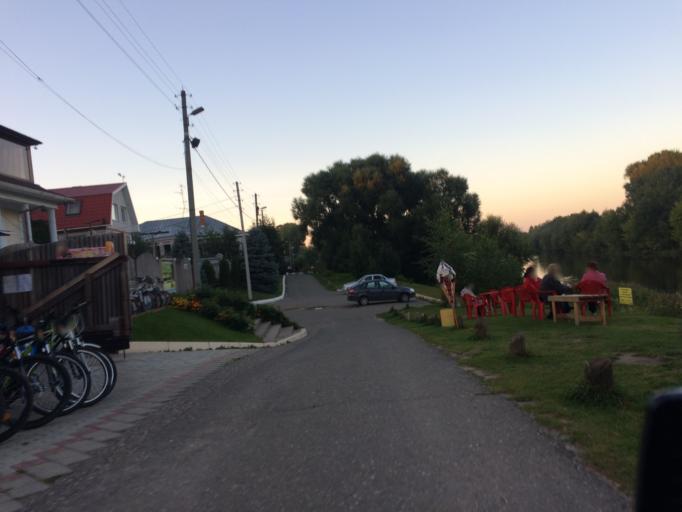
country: RU
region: Mariy-El
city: Yoshkar-Ola
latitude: 56.6405
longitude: 47.9057
